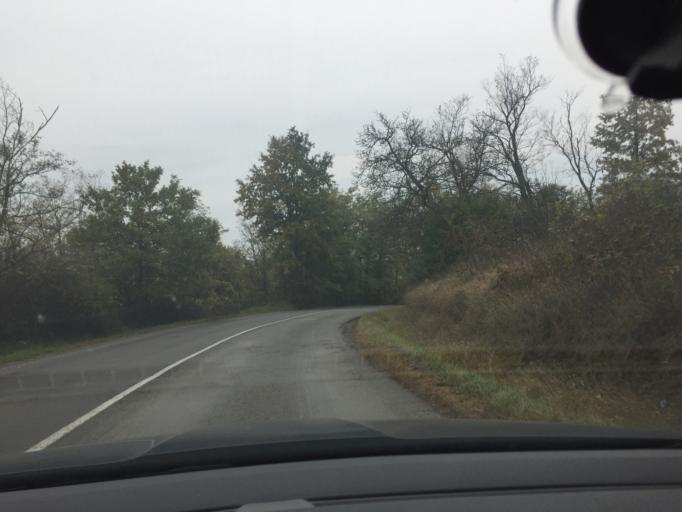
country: SK
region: Banskobystricky
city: Velky Krtis
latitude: 48.2170
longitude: 19.3696
